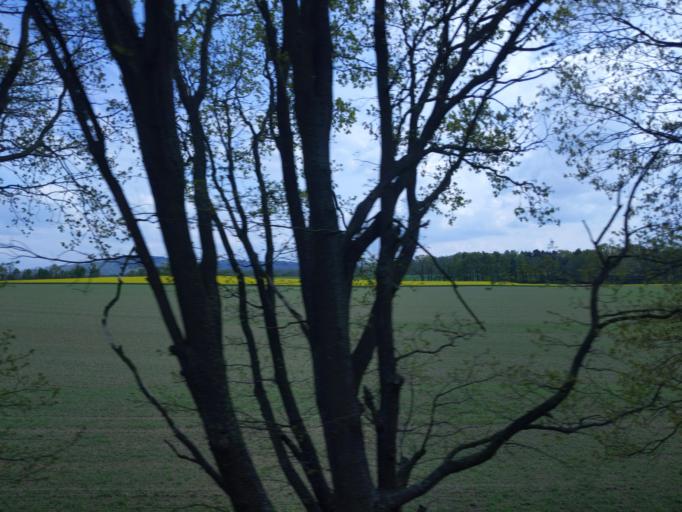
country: DE
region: Saxony
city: Goda
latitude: 51.1464
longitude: 14.3040
